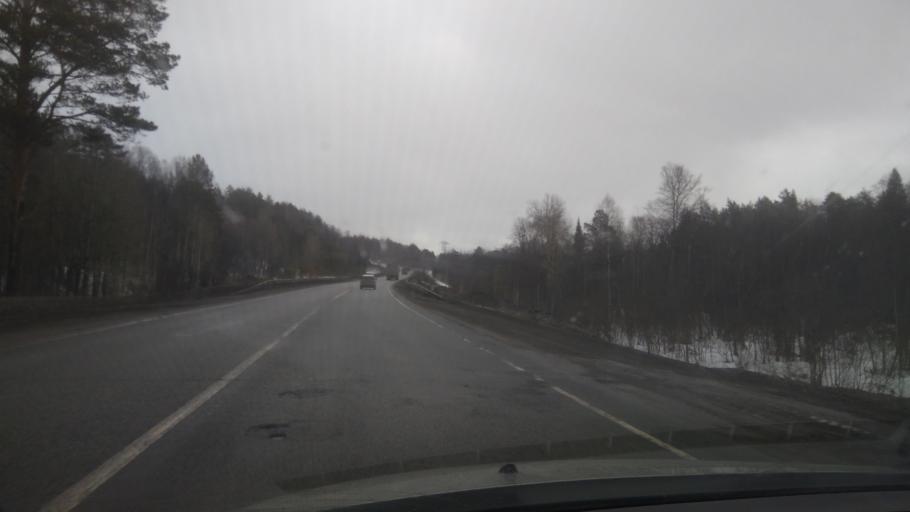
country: RU
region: Sverdlovsk
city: Ufimskiy
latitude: 56.7755
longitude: 58.2325
